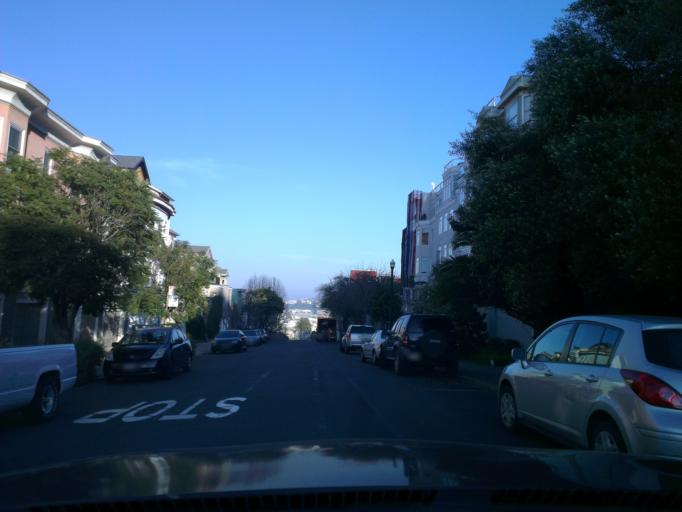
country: US
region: California
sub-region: San Francisco County
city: San Francisco
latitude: 37.7595
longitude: -122.4304
